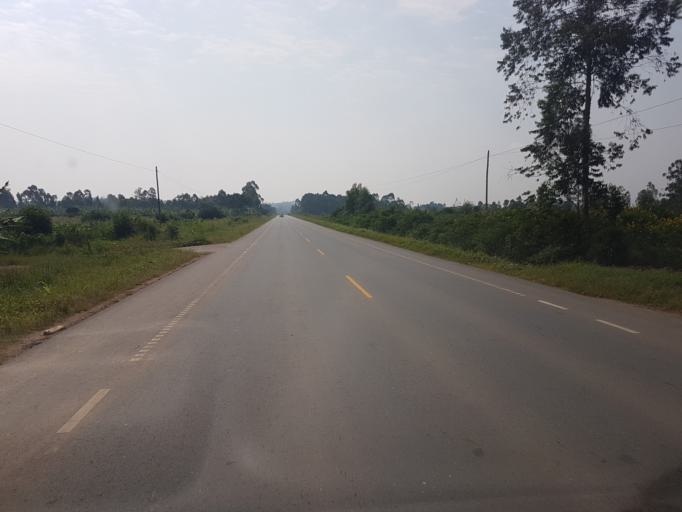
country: UG
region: Western Region
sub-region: Mbarara District
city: Bwizibwera
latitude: -0.6427
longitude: 30.5667
